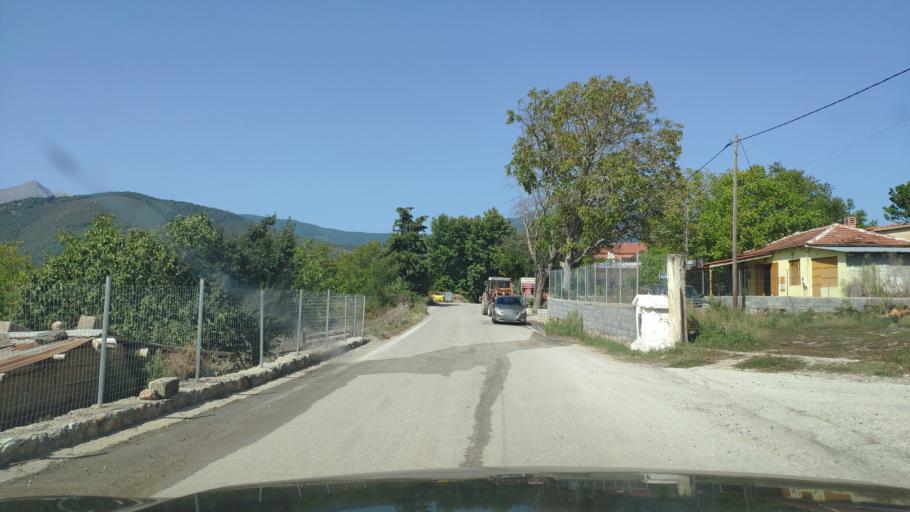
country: GR
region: West Greece
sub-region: Nomos Achaias
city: Aiyira
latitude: 37.9096
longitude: 22.3313
